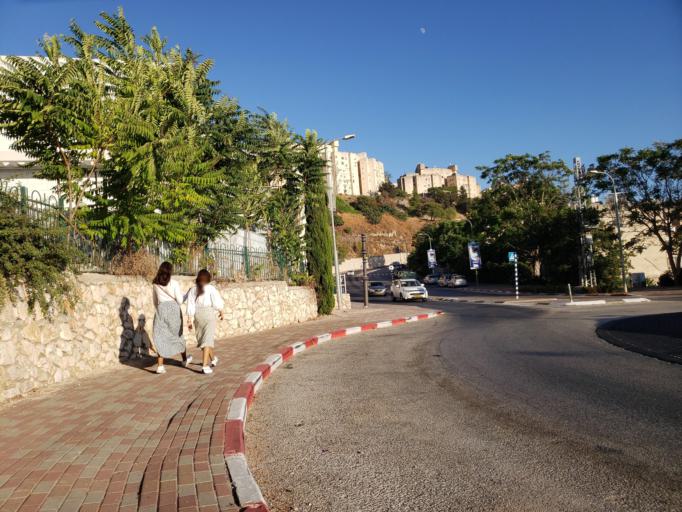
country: IL
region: Northern District
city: Safed
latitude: 32.9640
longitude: 35.4891
